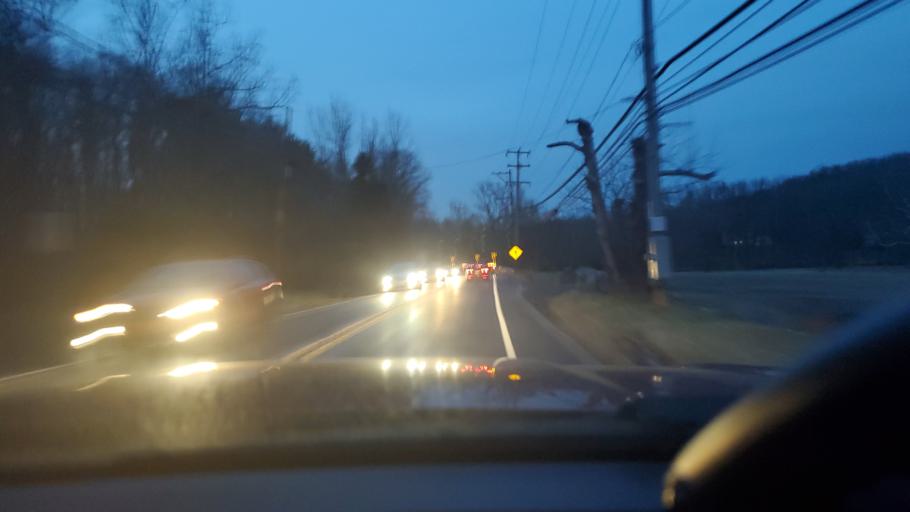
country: US
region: Pennsylvania
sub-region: Montgomery County
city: Spring Mount
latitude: 40.2701
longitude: -75.4712
